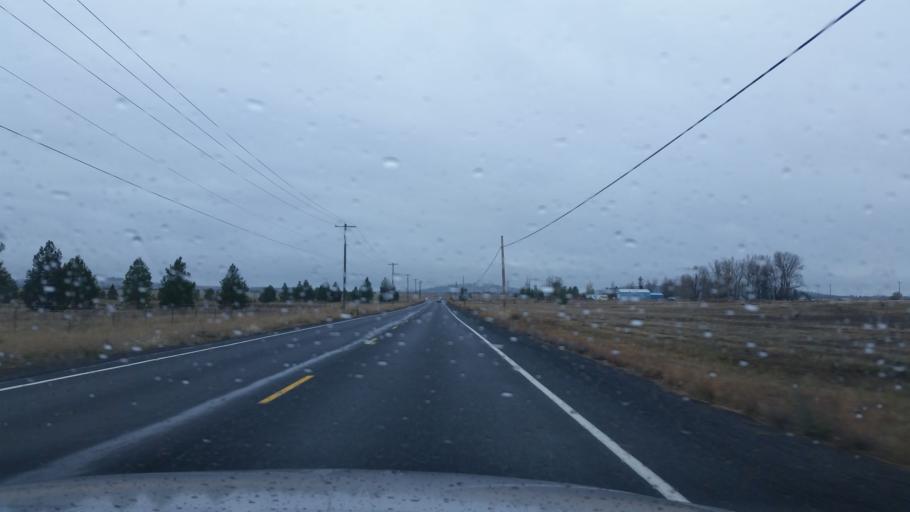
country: US
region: Washington
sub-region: Spokane County
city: Airway Heights
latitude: 47.6185
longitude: -117.6041
